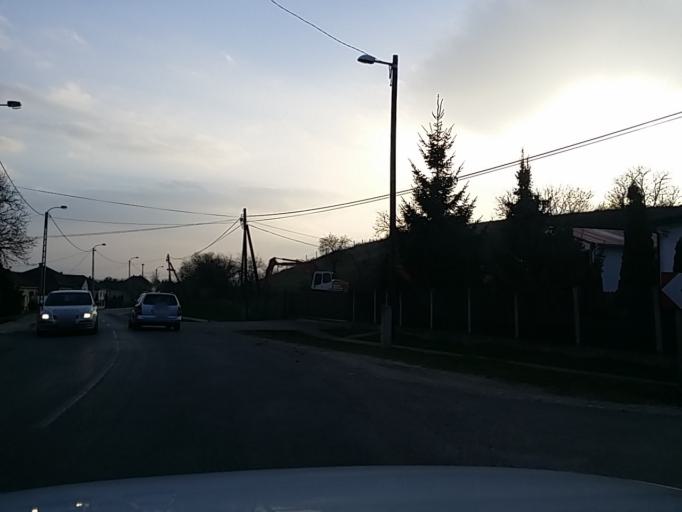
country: HU
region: Heves
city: Tarnalelesz
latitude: 48.0527
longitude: 20.1575
